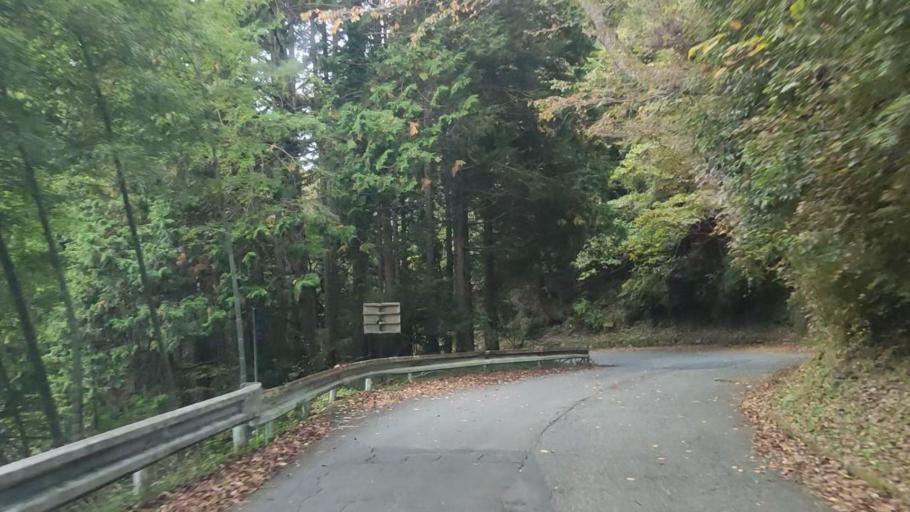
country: JP
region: Shizuoka
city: Ito
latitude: 34.9549
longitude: 139.0489
